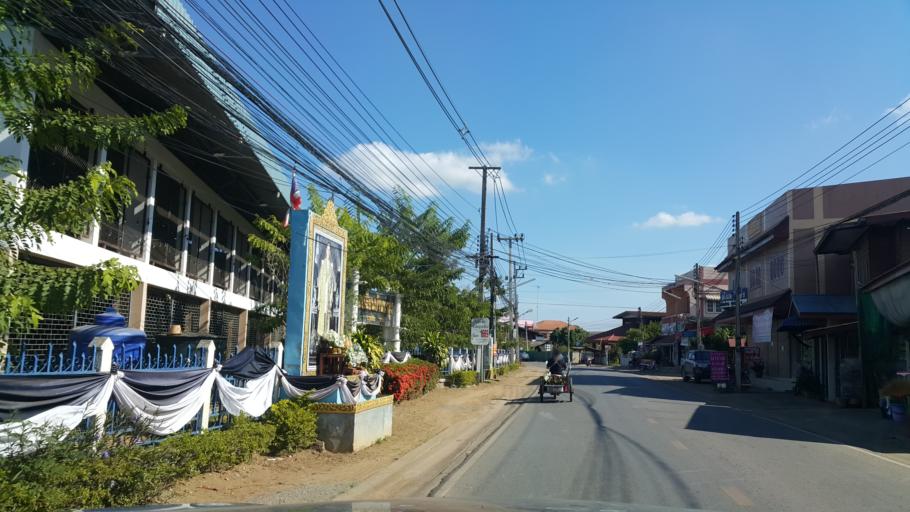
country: TH
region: Sukhothai
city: Thung Saliam
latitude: 17.3178
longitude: 99.5496
